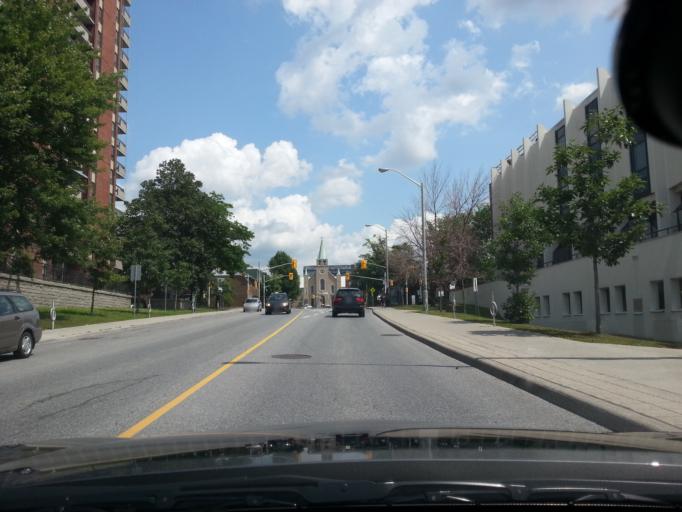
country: CA
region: Ontario
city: Ottawa
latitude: 45.4050
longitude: -75.7108
